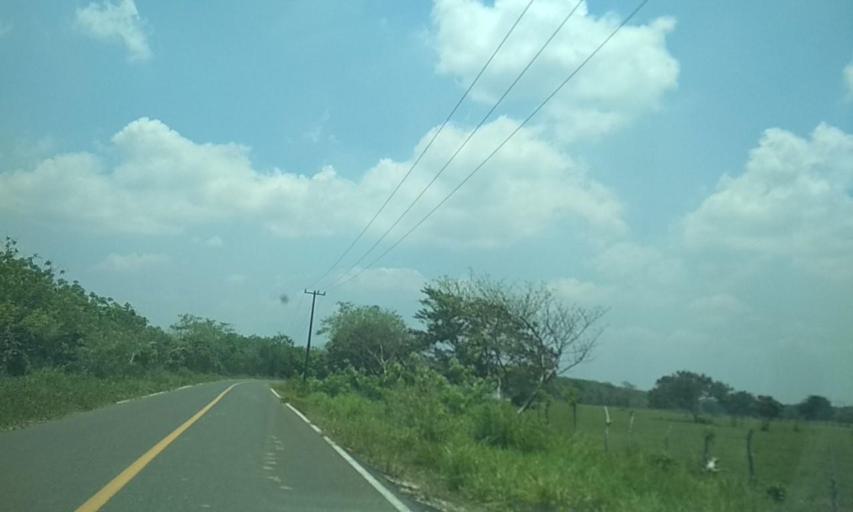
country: MX
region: Tabasco
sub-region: Huimanguillo
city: Francisco Rueda
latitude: 17.7576
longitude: -94.0523
